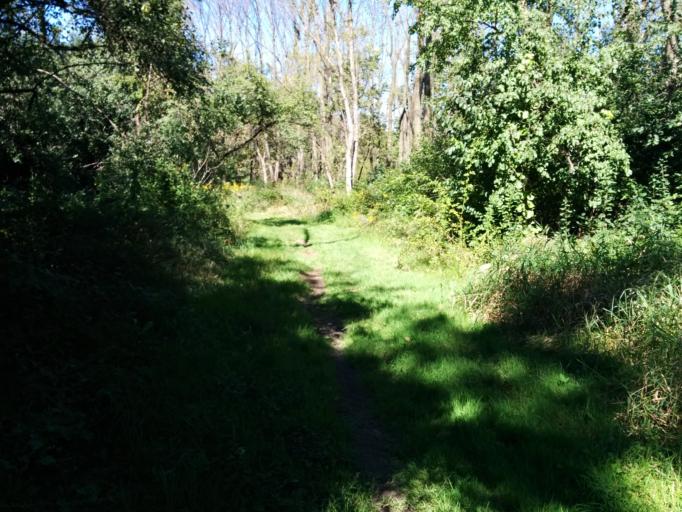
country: US
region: Illinois
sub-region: Cook County
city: Western Springs
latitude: 41.8221
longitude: -87.9137
